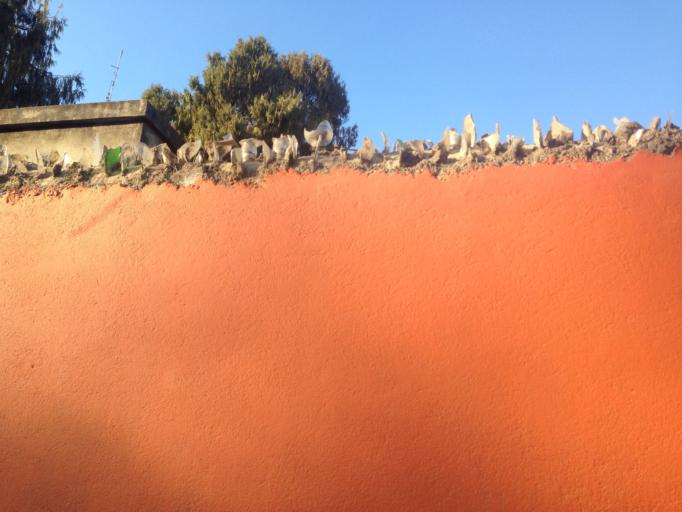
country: NP
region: Central Region
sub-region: Bagmati Zone
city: Kathmandu
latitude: 27.7181
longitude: 85.3200
